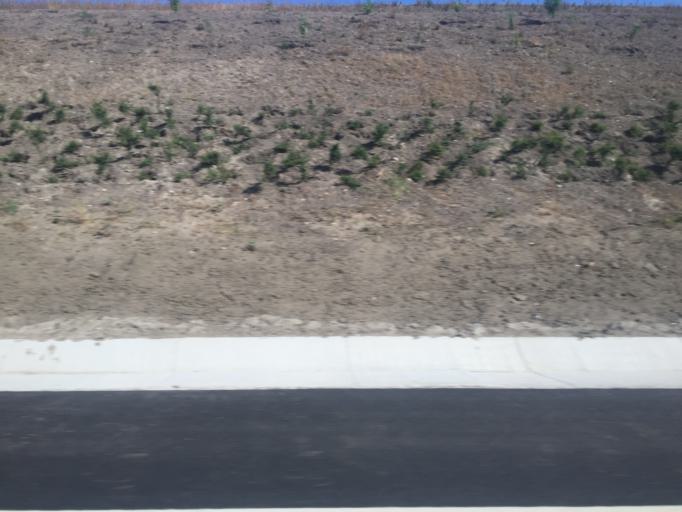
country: TR
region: Bursa
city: Mahmudiye
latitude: 40.2571
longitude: 28.7223
